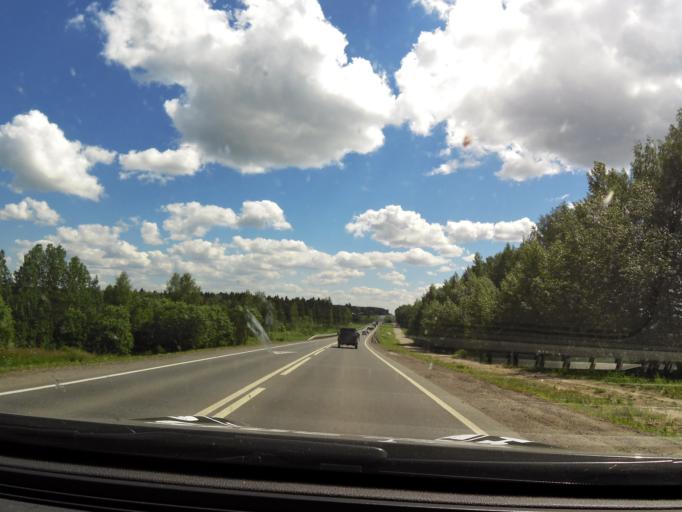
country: RU
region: Vologda
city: Molochnoye
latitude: 59.2845
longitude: 39.6979
